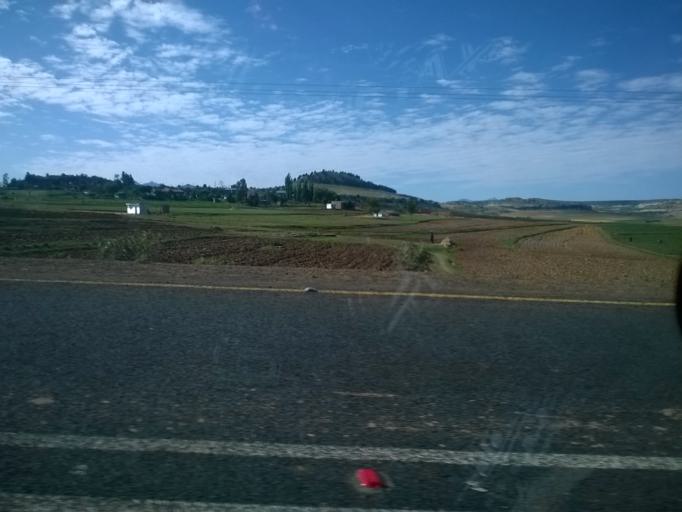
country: LS
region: Berea
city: Teyateyaneng
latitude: -29.0922
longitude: 27.9361
